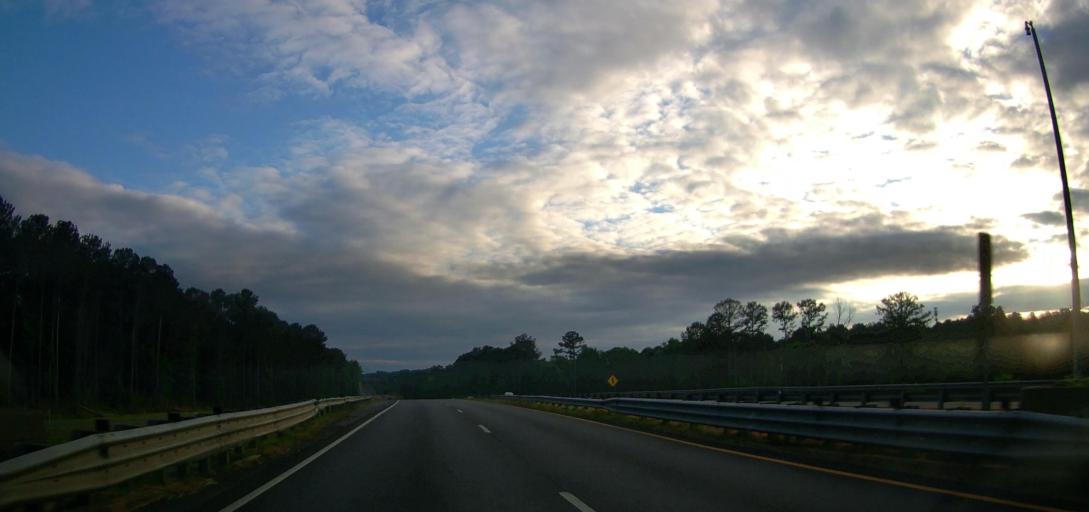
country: US
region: Georgia
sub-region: Clarke County
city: Country Club Estates
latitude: 33.9641
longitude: -83.4282
